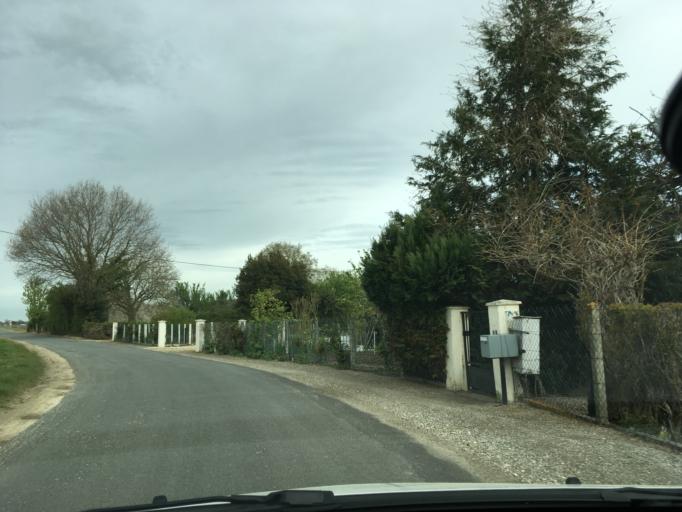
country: FR
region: Aquitaine
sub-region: Departement de la Gironde
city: Lesparre-Medoc
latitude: 45.3245
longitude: -0.8798
